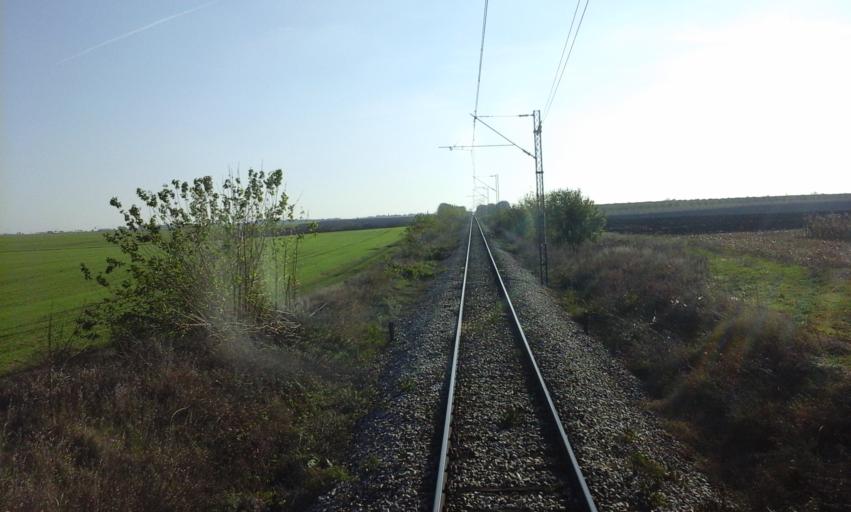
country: RS
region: Autonomna Pokrajina Vojvodina
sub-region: Severnobacki Okrug
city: Backa Topola
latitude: 45.7698
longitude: 19.6482
